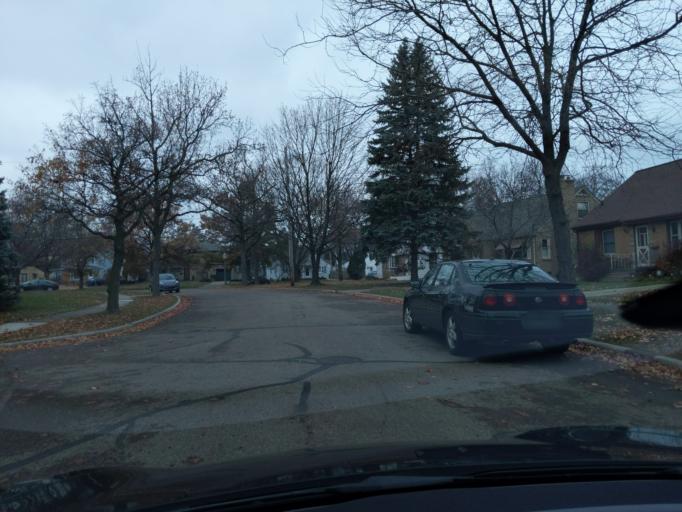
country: US
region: Michigan
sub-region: Ingham County
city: Lansing
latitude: 42.7088
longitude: -84.5800
